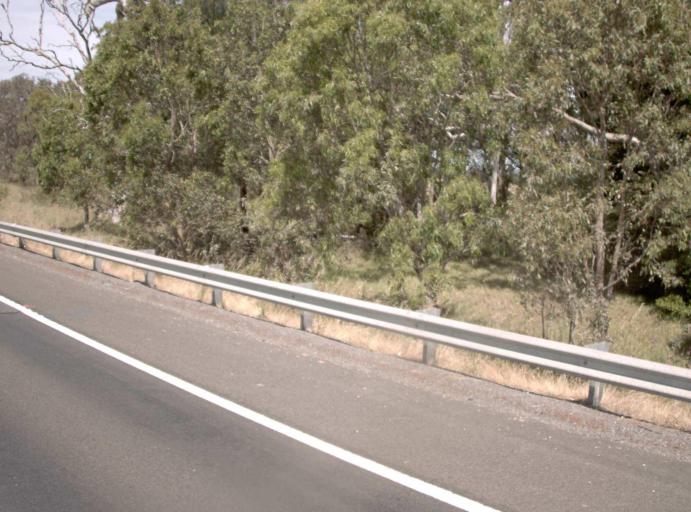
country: AU
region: Victoria
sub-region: East Gippsland
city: Bairnsdale
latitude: -37.8958
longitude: 147.3699
